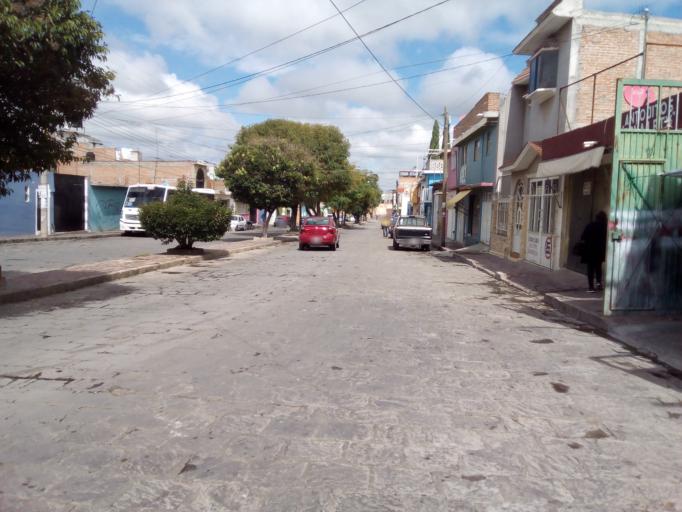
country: MX
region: Guerrero
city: San Luis de la Paz
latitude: 21.2954
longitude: -100.5118
